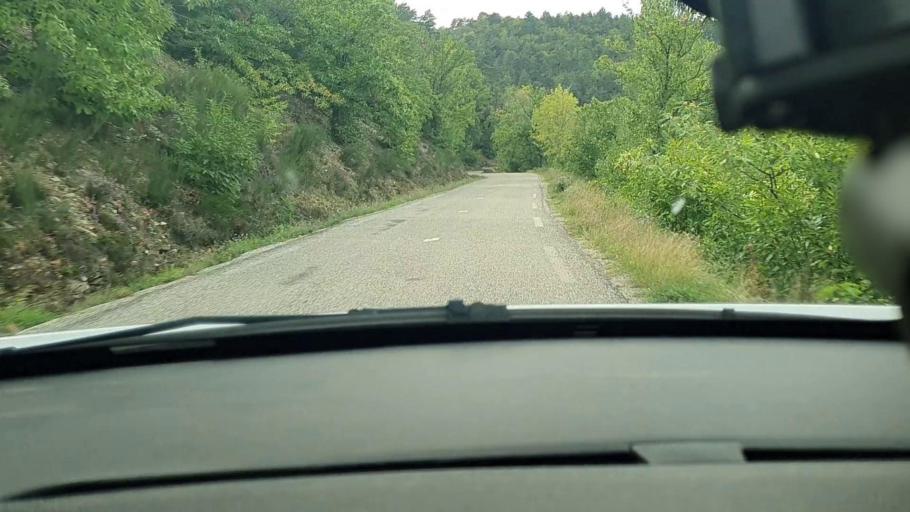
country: FR
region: Languedoc-Roussillon
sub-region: Departement du Gard
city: Branoux-les-Taillades
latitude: 44.2852
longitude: 3.9770
